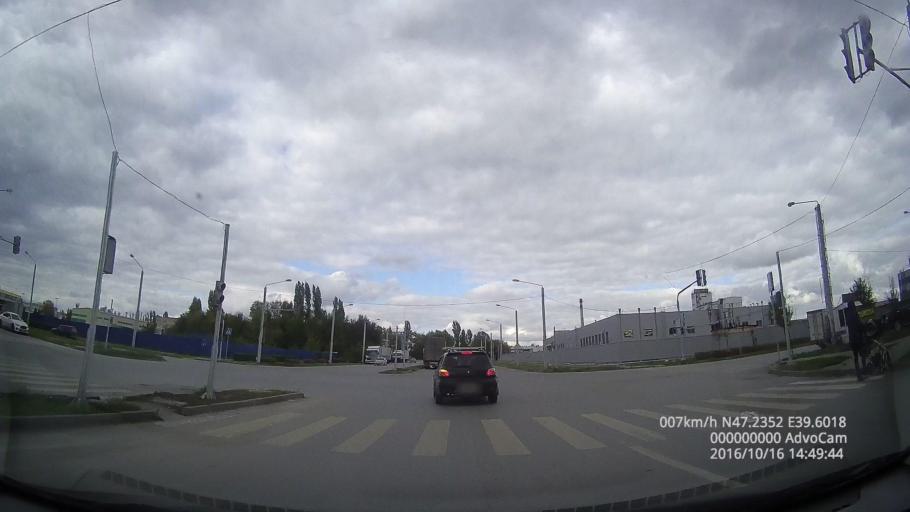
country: RU
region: Rostov
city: Kalinin
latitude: 47.2359
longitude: 39.5985
